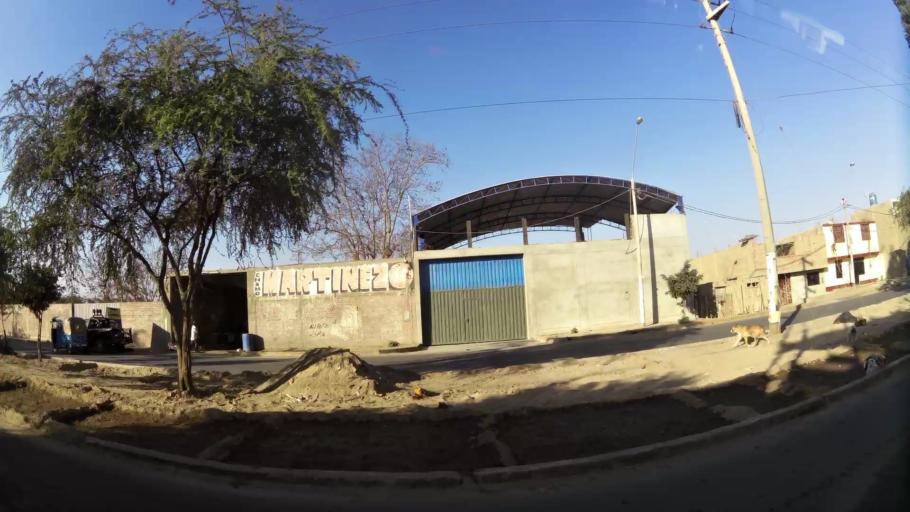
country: PE
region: Ica
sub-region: Provincia de Ica
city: Ica
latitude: -14.0679
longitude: -75.7191
